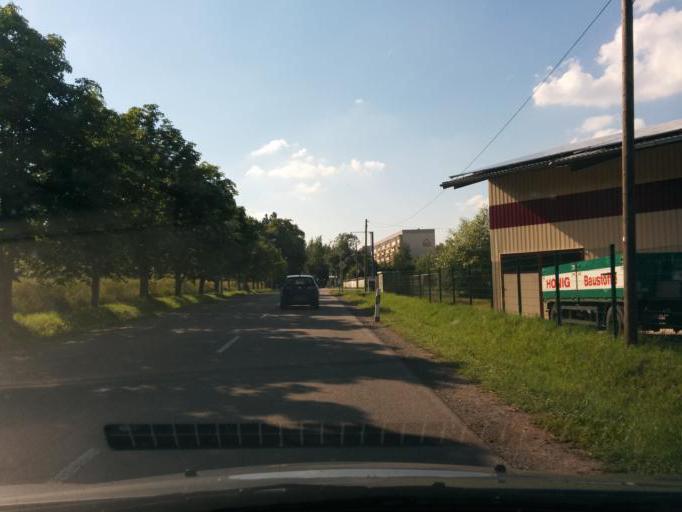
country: DE
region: Saxony
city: Floha
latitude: 50.8453
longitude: 13.0751
